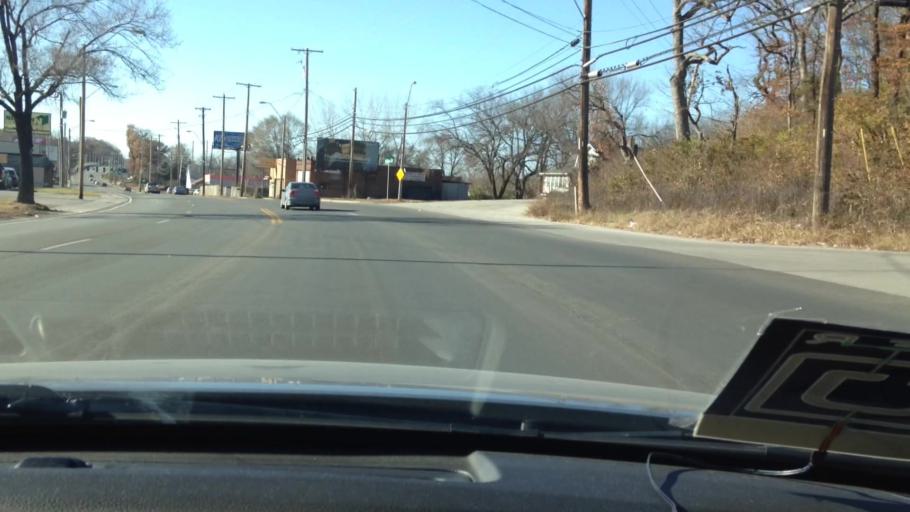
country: US
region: Missouri
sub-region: Jackson County
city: Raytown
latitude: 39.0347
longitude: -94.5178
